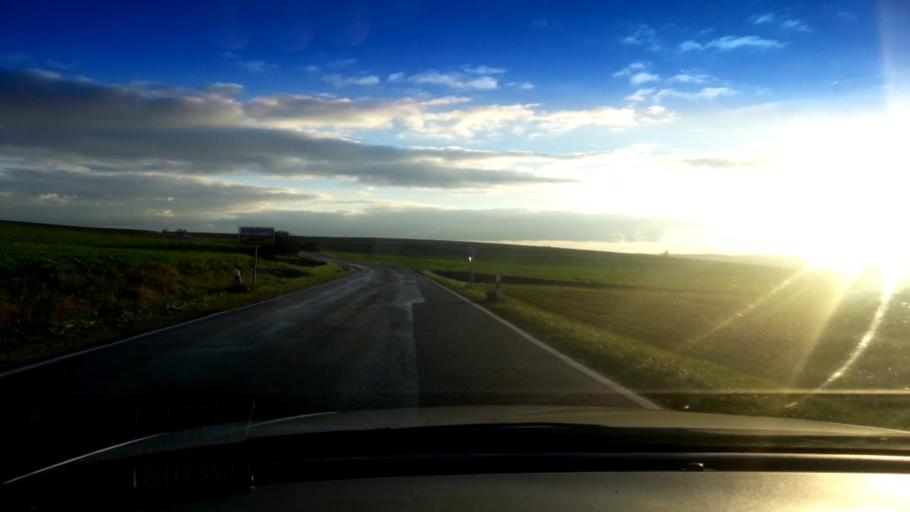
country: DE
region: Bavaria
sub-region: Upper Franconia
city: Buttenheim
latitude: 49.8360
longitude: 11.0303
